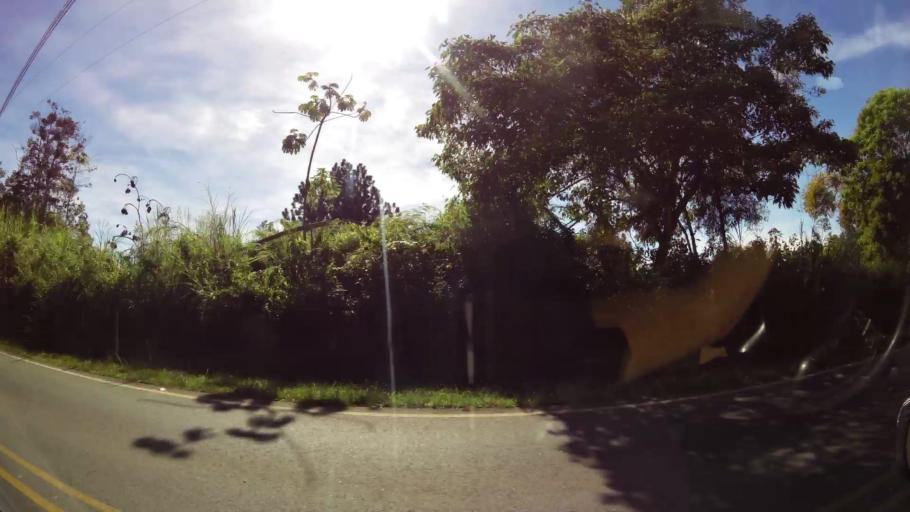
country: CR
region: San Jose
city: San Isidro
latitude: 9.4148
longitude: -83.7127
